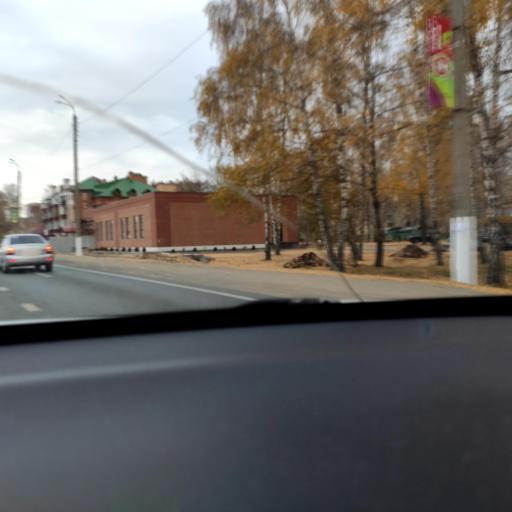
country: RU
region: Tatarstan
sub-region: Zelenodol'skiy Rayon
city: Zelenodolsk
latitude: 55.8474
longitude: 48.5583
